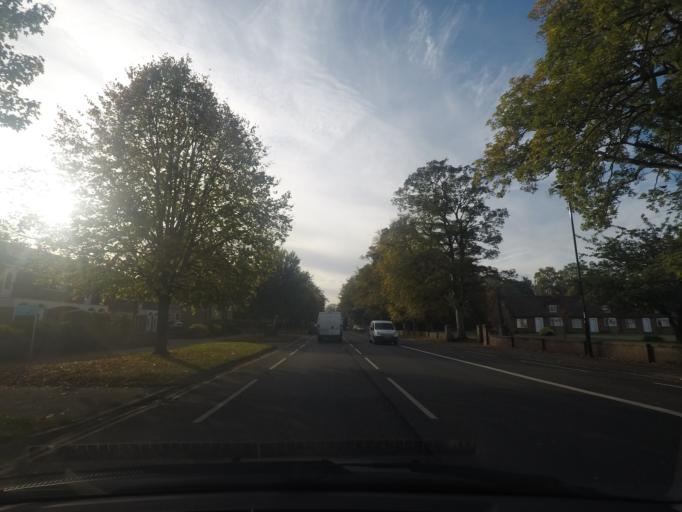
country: GB
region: England
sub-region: City of York
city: Fulford
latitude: 53.9395
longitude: -1.0740
